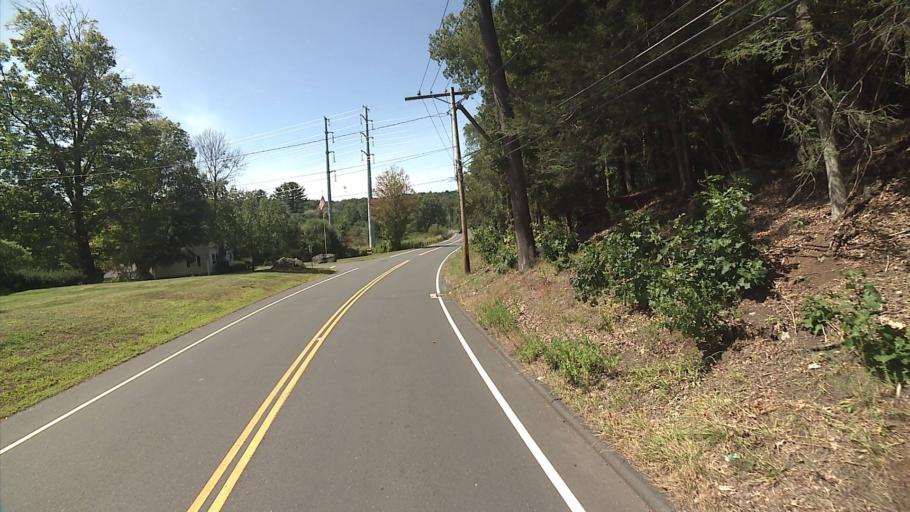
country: US
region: Connecticut
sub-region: New Haven County
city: Middlebury
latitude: 41.5271
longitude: -73.0926
